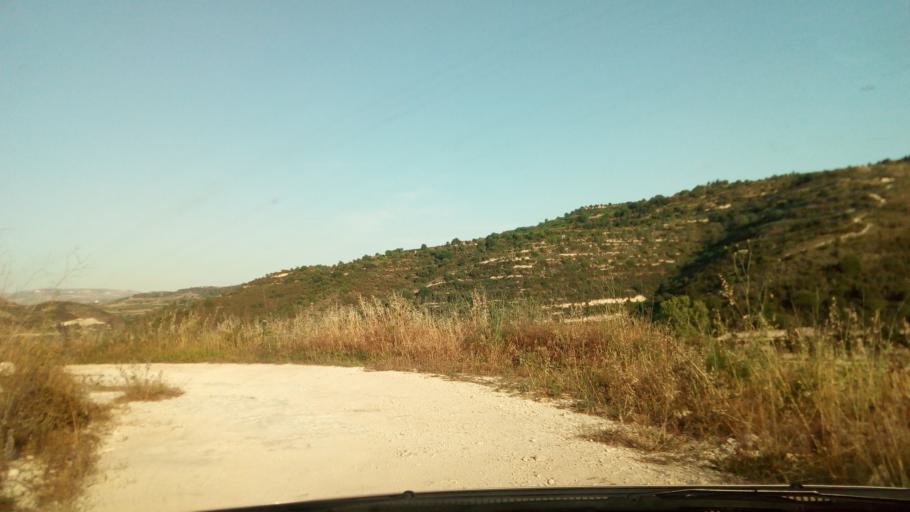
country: CY
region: Pafos
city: Tala
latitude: 34.8716
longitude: 32.4655
